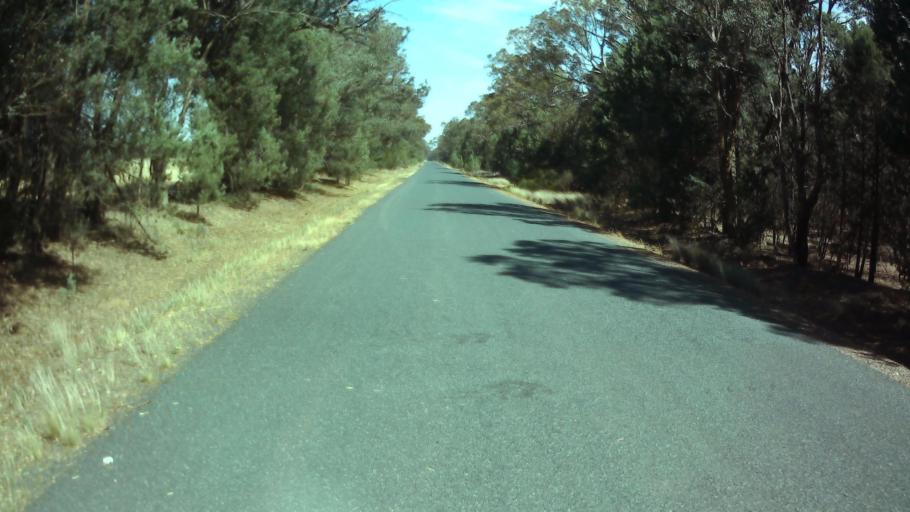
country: AU
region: New South Wales
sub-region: Weddin
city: Grenfell
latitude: -34.0585
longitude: 148.1314
